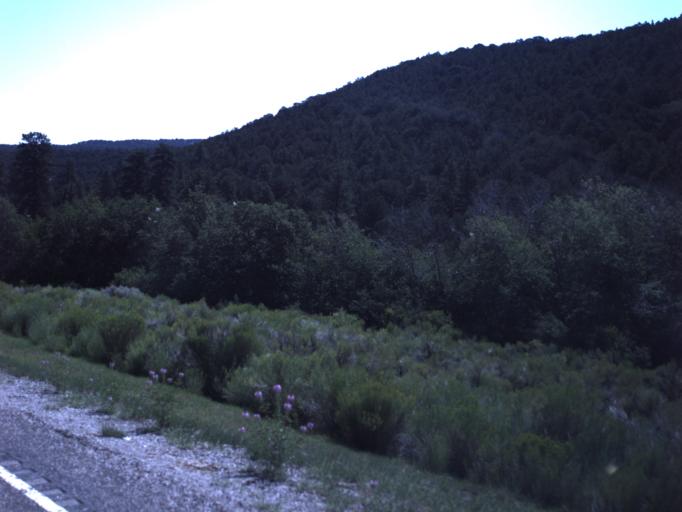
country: US
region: Utah
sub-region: Wayne County
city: Loa
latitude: 38.6499
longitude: -111.4392
